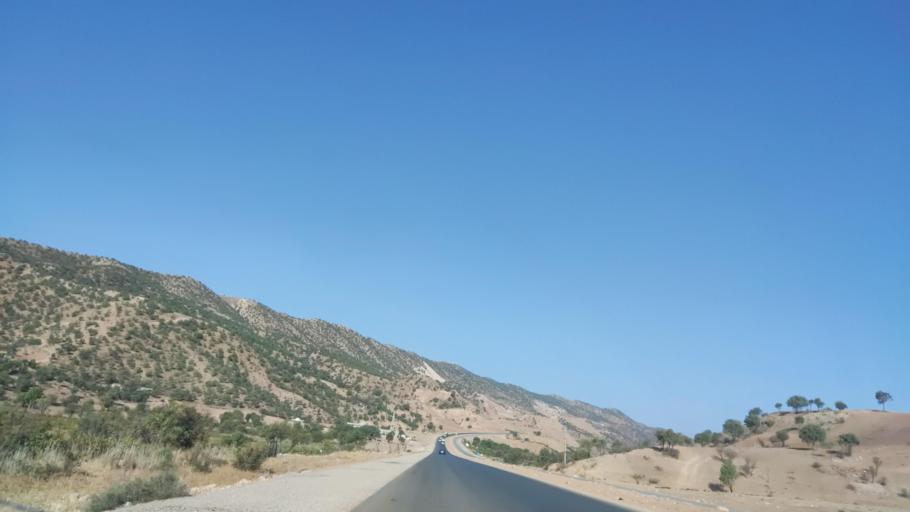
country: IQ
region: Arbil
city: Shaqlawah
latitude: 36.4305
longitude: 44.3226
